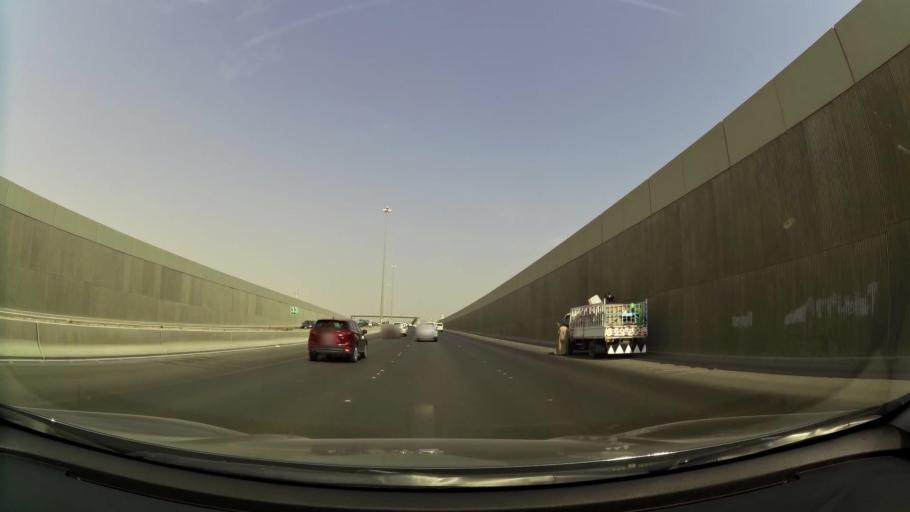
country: KW
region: Al Ahmadi
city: Al Manqaf
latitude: 29.1078
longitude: 48.1184
